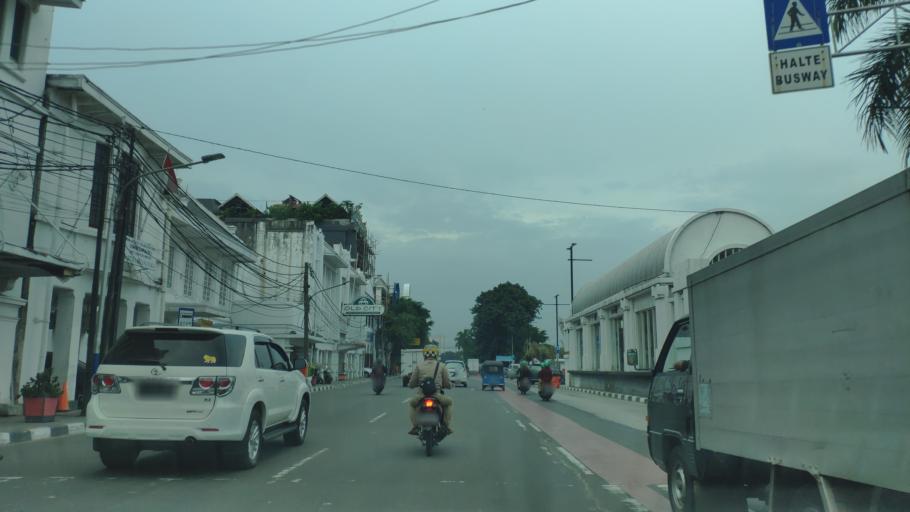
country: ID
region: Jakarta Raya
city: Jakarta
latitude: -6.1360
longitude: 106.8118
